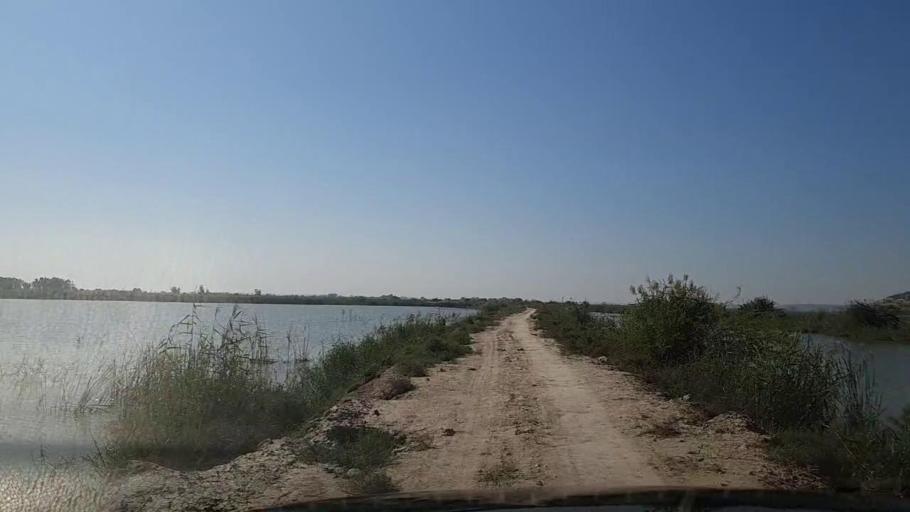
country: PK
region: Sindh
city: Thatta
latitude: 24.6762
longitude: 67.8893
